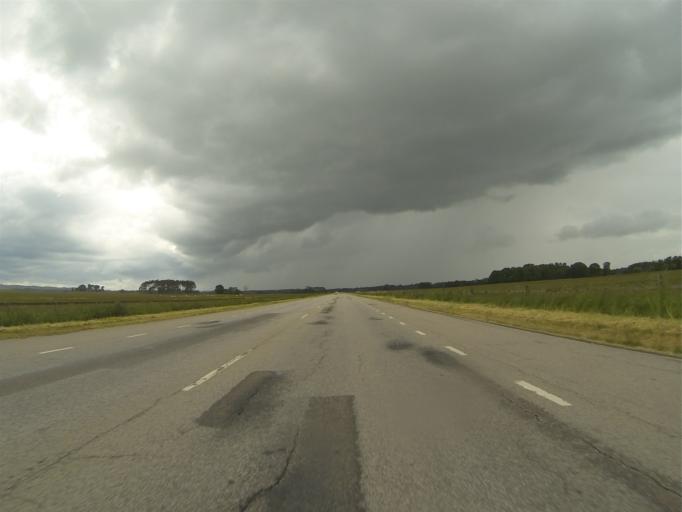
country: SE
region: Skane
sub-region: Hoors Kommun
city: Loberod
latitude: 55.7265
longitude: 13.4417
